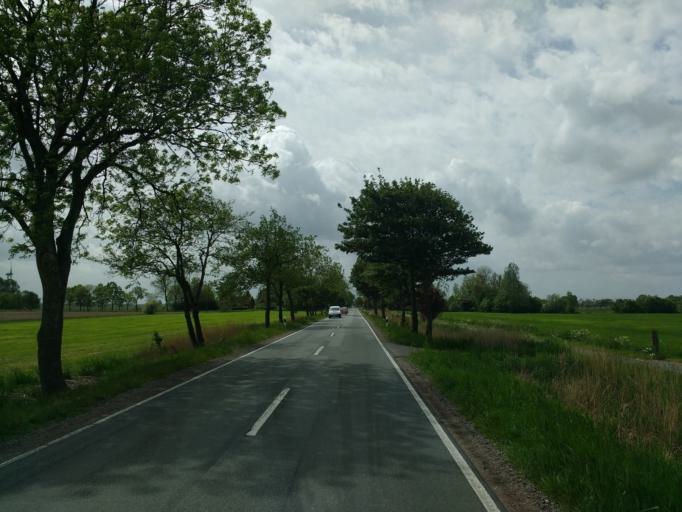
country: DE
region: Lower Saxony
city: Jever
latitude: 53.6046
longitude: 7.9267
